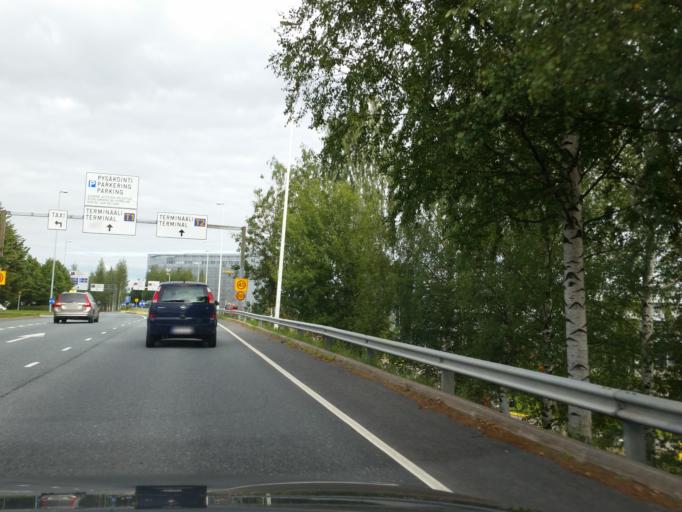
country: FI
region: Uusimaa
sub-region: Helsinki
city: Vantaa
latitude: 60.3114
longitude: 24.9706
